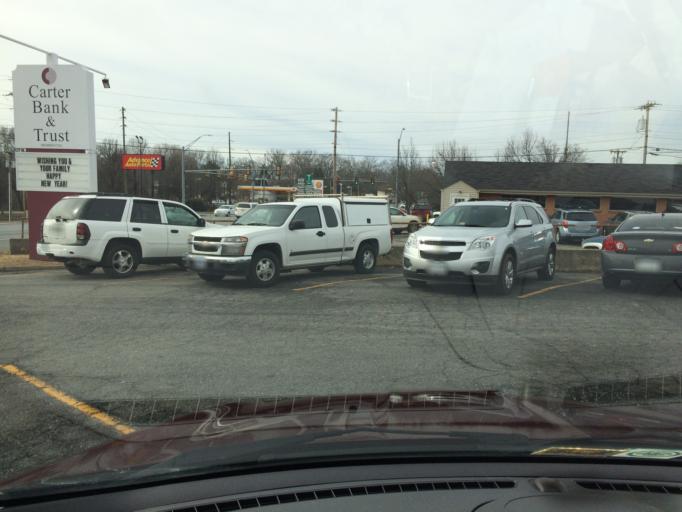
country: US
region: Virginia
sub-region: City of Bedford
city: Bedford
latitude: 37.3484
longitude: -79.5030
